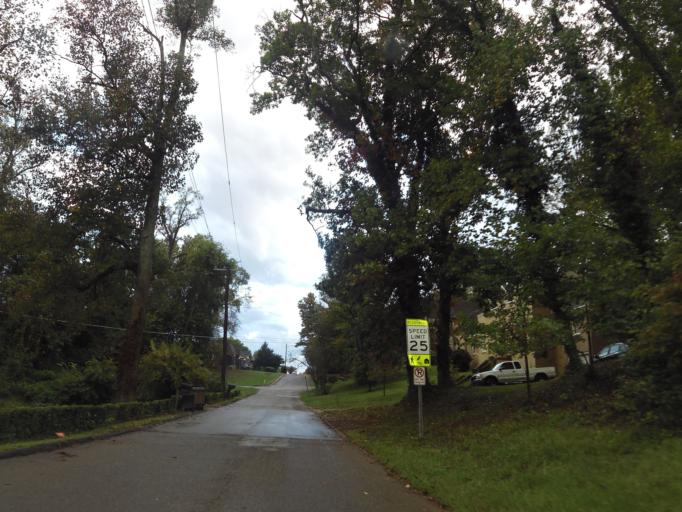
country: US
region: Tennessee
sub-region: Knox County
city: Knoxville
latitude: 35.9974
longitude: -83.8868
